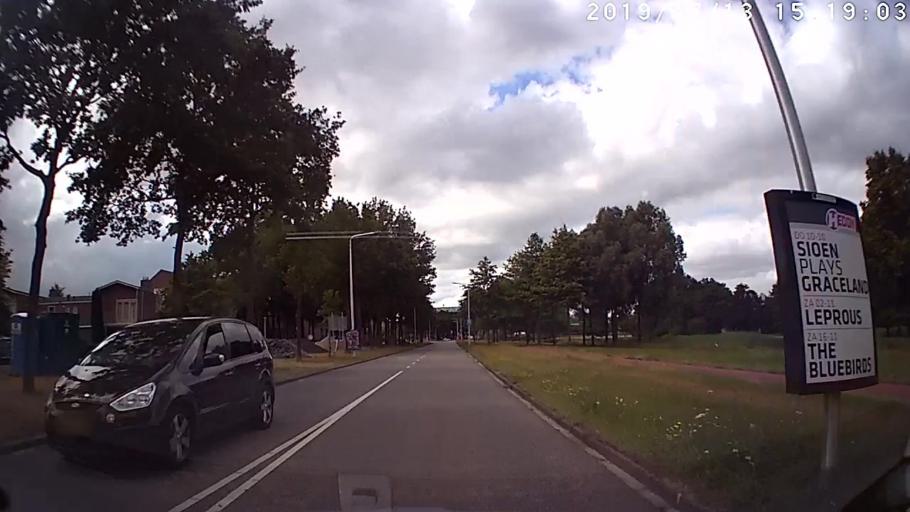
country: NL
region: Overijssel
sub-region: Gemeente Zwolle
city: Zwolle
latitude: 52.5060
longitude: 6.1095
